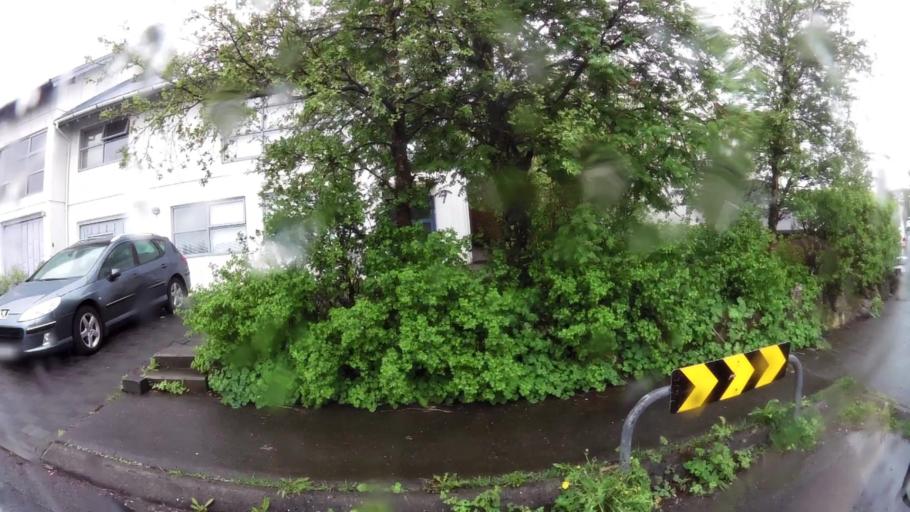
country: IS
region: Capital Region
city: Reykjavik
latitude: 64.0987
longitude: -21.8405
